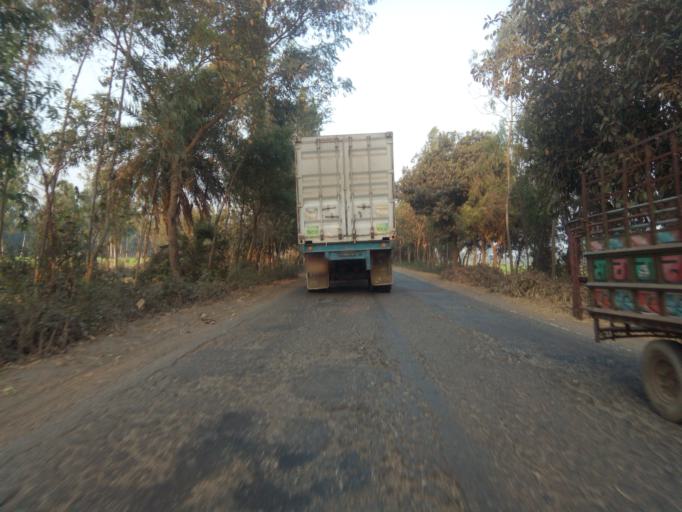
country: BD
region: Rajshahi
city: Bogra
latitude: 24.5602
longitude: 89.2020
